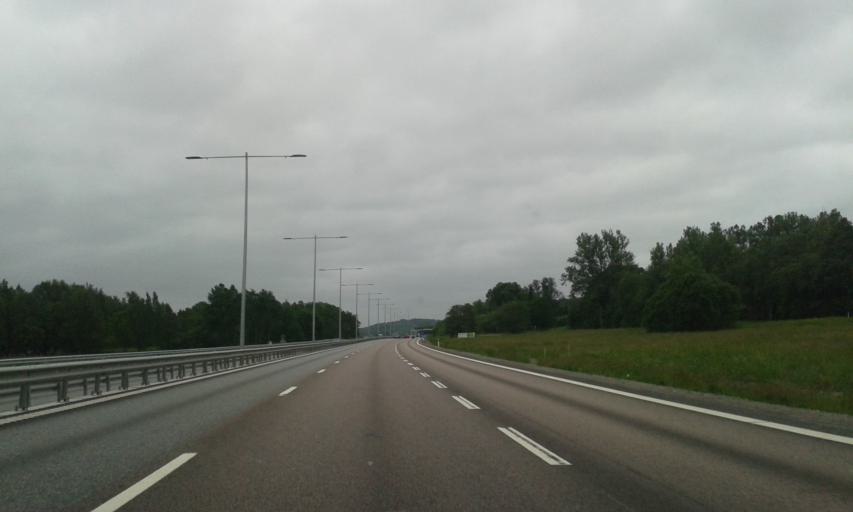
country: SE
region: Vaestra Goetaland
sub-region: Ale Kommun
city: Surte
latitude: 57.8377
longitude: 12.0059
